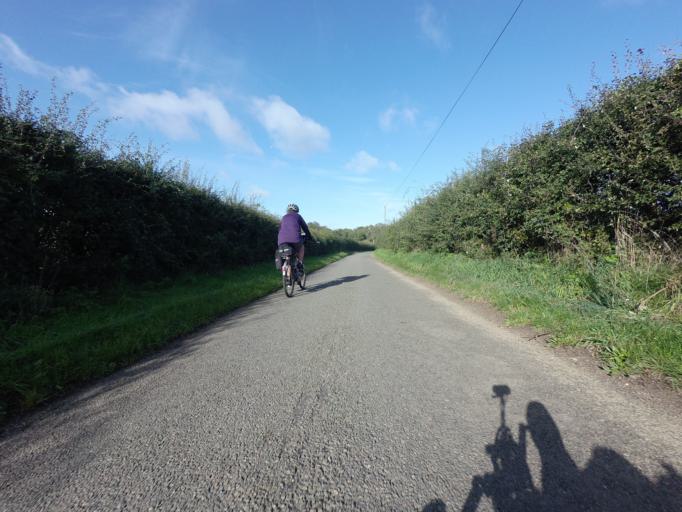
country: GB
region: England
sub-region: Norfolk
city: Dersingham
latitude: 52.8483
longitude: 0.6741
